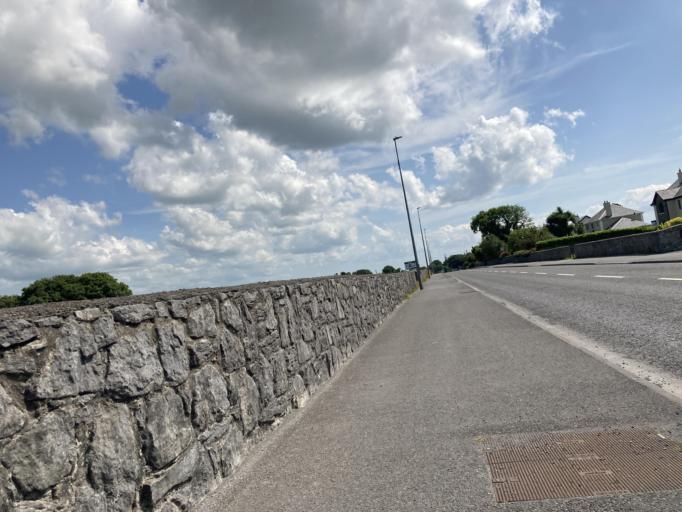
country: IE
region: Connaught
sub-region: County Galway
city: Claregalway
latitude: 53.2966
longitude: -8.9857
